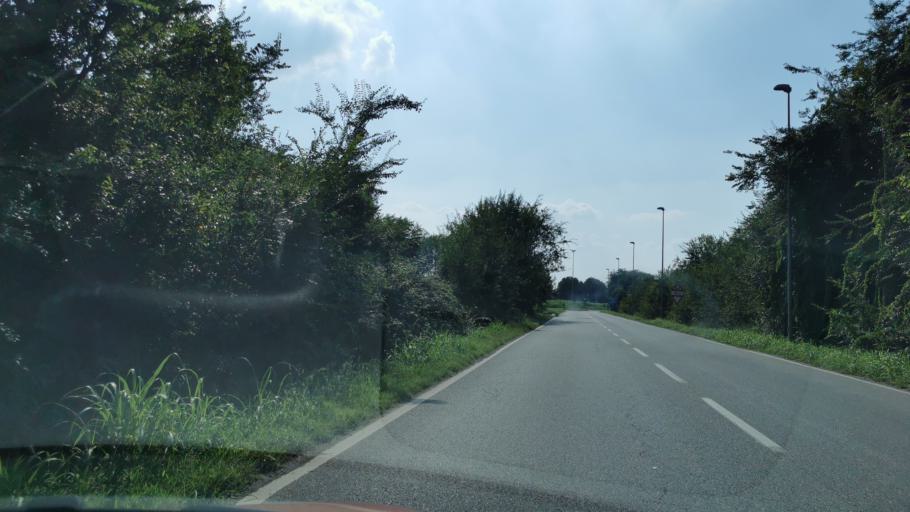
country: IT
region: Lombardy
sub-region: Provincia di Monza e Brianza
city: Muggio
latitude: 45.5843
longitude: 9.2137
